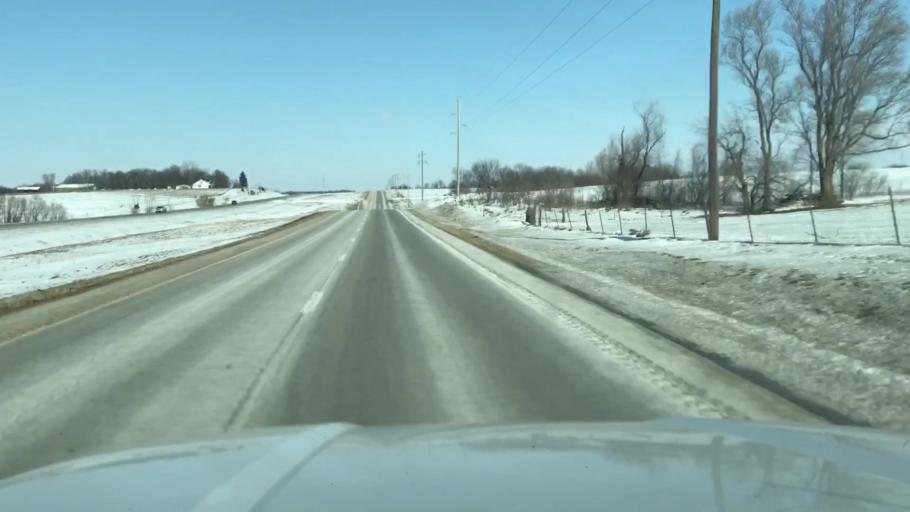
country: US
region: Missouri
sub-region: Nodaway County
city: Maryville
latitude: 40.1530
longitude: -94.8691
